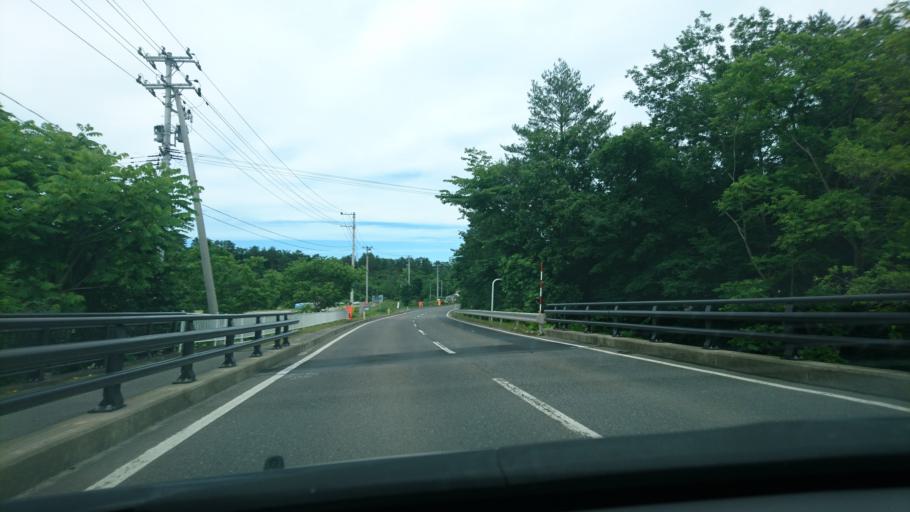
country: JP
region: Iwate
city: Miyako
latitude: 39.9527
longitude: 141.8425
